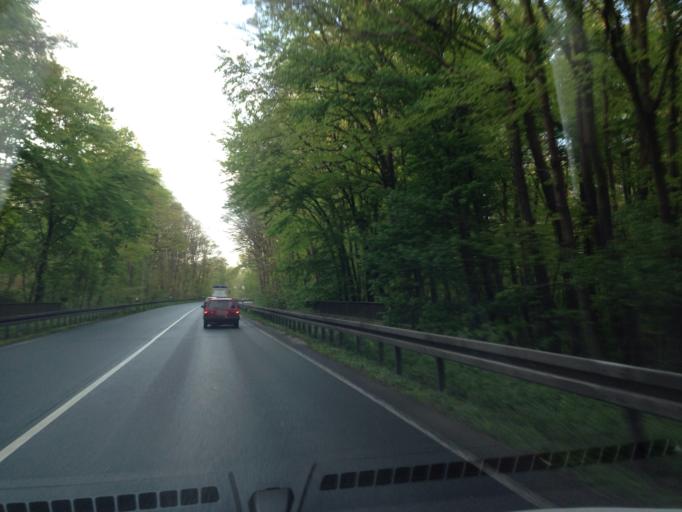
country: DE
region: North Rhine-Westphalia
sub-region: Regierungsbezirk Munster
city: Muenster
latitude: 51.9679
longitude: 7.6737
